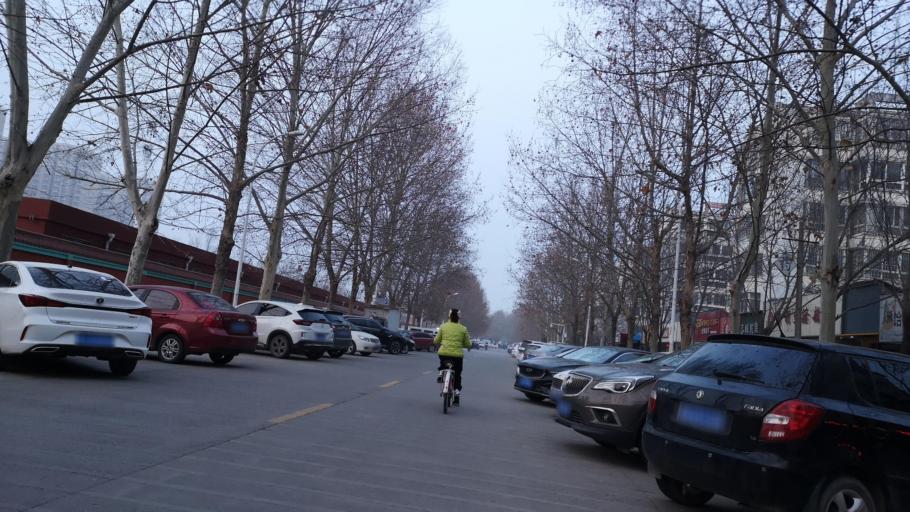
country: CN
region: Henan Sheng
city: Zhongyuanlu
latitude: 35.7550
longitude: 115.0611
